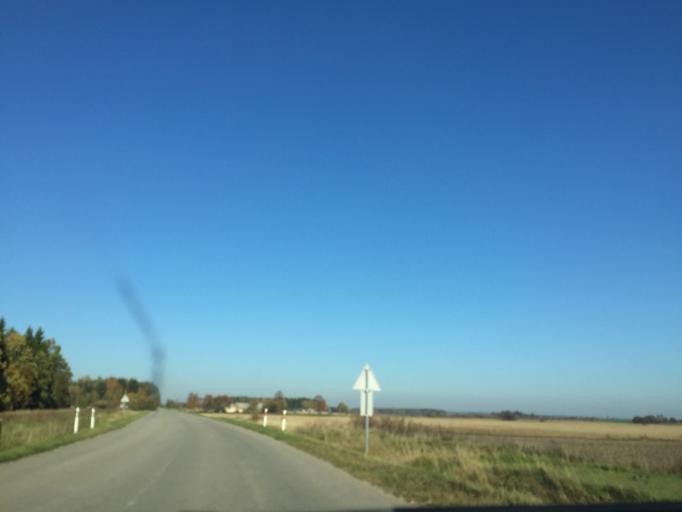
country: LT
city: Salantai
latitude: 55.9609
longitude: 21.6523
